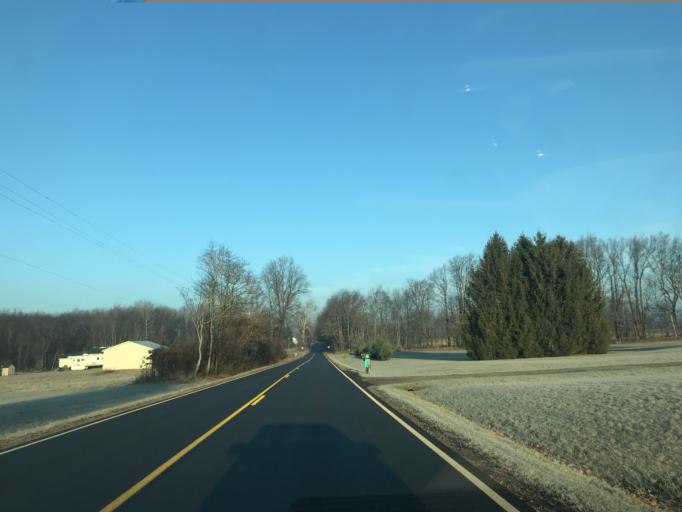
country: US
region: Michigan
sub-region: Ingham County
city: Leslie
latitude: 42.4278
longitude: -84.5282
